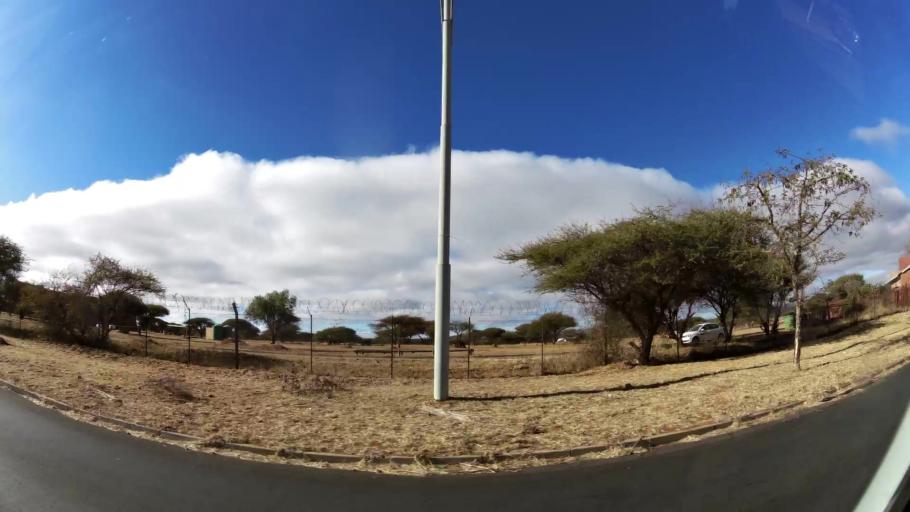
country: ZA
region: Limpopo
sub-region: Capricorn District Municipality
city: Polokwane
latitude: -23.9258
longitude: 29.4700
